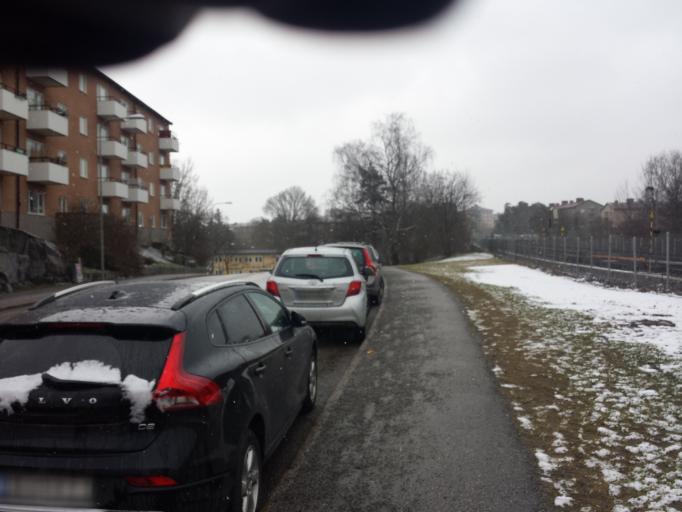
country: SE
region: Stockholm
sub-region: Nacka Kommun
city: Nacka
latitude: 59.2896
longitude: 18.1158
